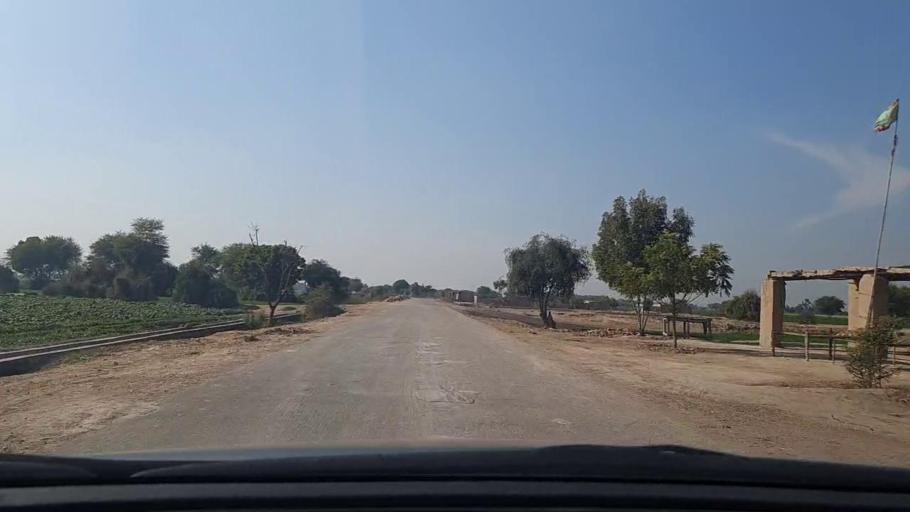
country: PK
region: Sindh
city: Daulatpur
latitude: 26.3140
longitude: 68.0695
